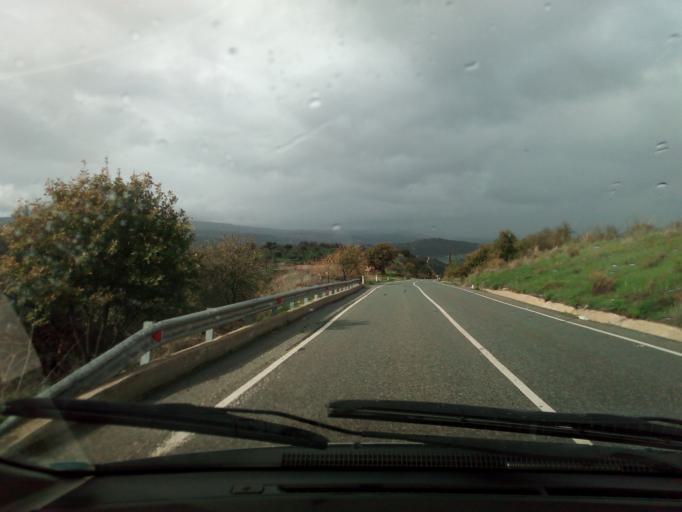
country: CY
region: Pafos
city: Polis
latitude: 34.9465
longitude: 32.4979
